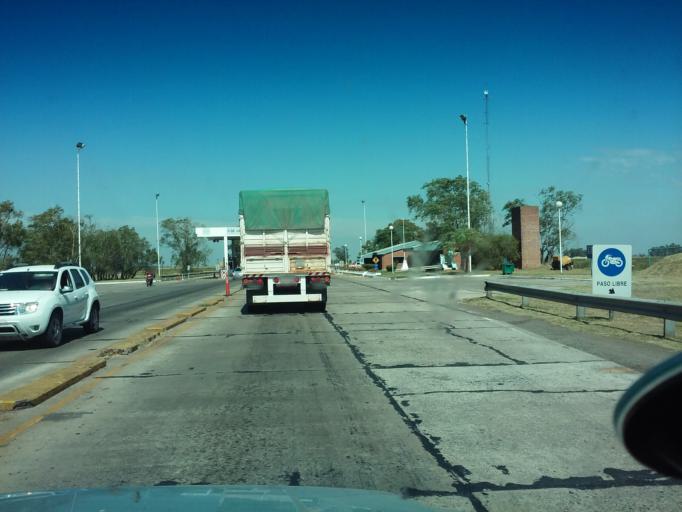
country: AR
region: Buenos Aires
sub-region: Partido de Nueve de Julio
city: Nueve de Julio
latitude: -35.3599
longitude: -60.7023
